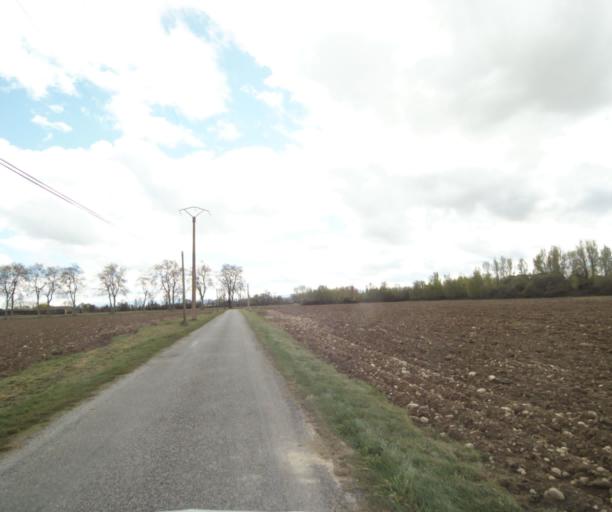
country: FR
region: Midi-Pyrenees
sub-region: Departement de l'Ariege
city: Saverdun
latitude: 43.2559
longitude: 1.5824
